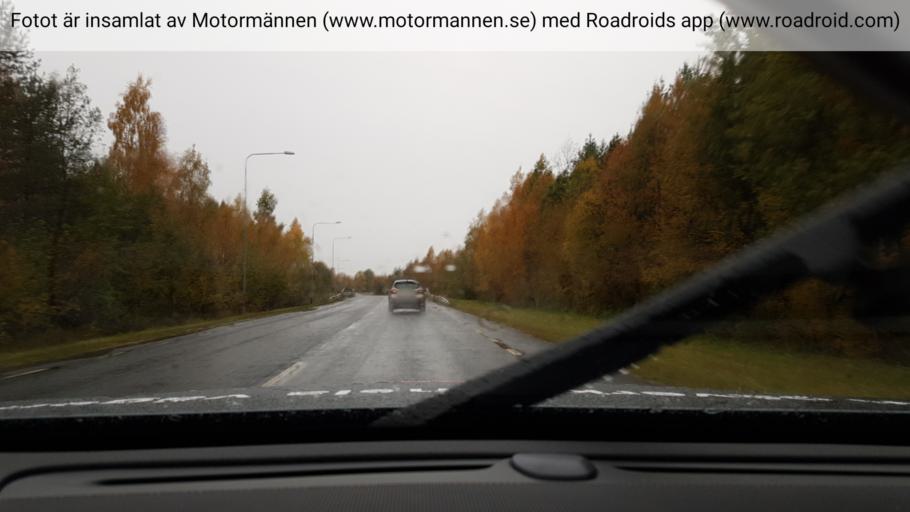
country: SE
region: Norrbotten
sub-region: Lulea Kommun
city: Gammelstad
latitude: 65.6540
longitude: 21.9779
